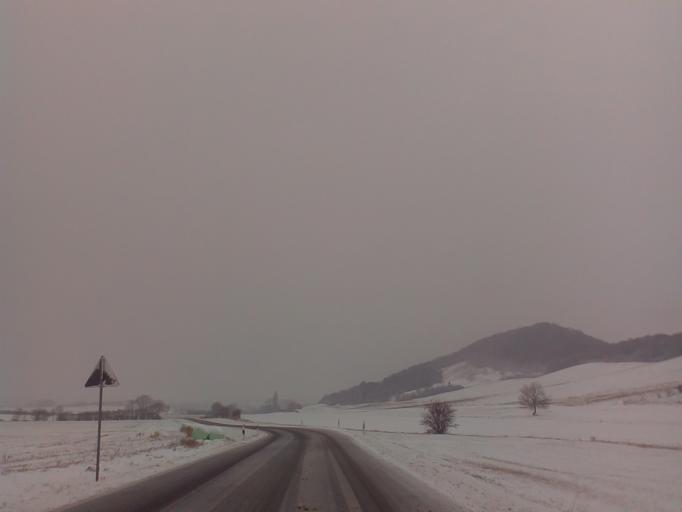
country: DE
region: Thuringia
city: Wandersleben
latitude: 50.8567
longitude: 10.8536
